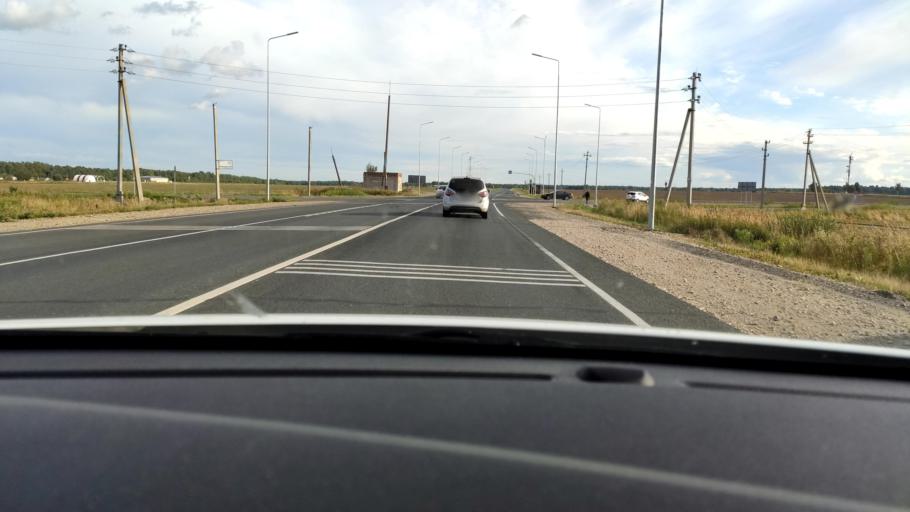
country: RU
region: Mariy-El
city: Suslonger
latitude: 56.2155
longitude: 48.2368
